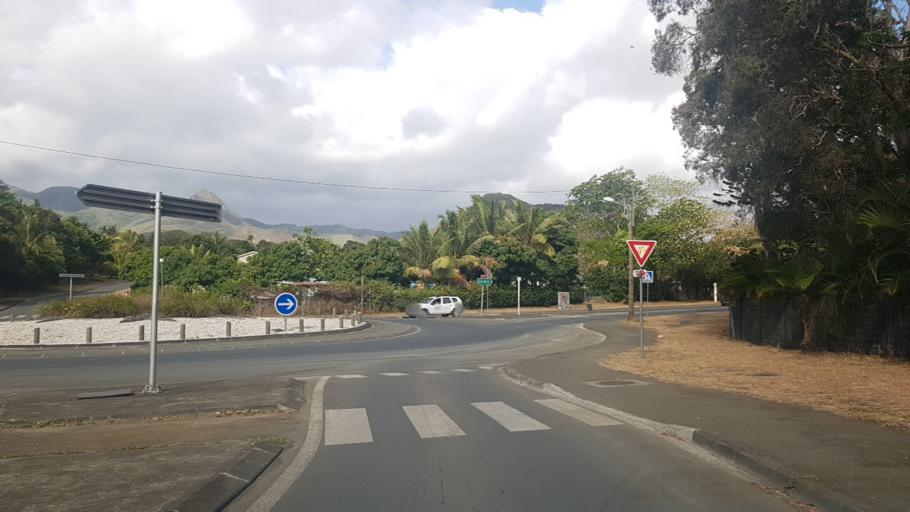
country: NC
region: South Province
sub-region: Noumea
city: Noumea
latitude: -22.2151
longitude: 166.4797
